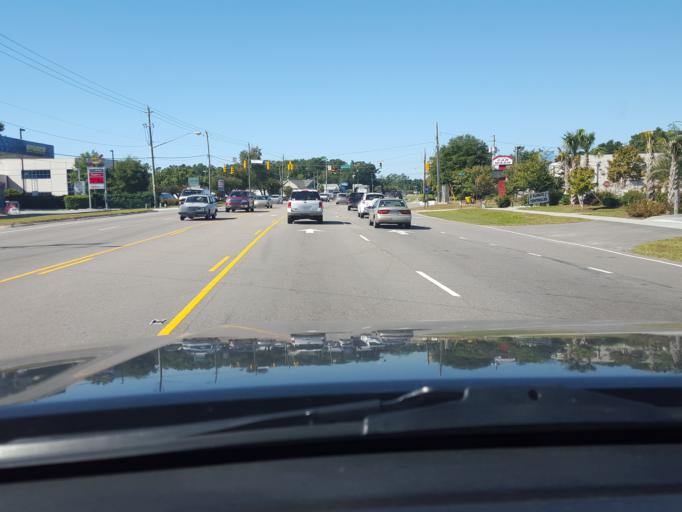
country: US
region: North Carolina
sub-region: New Hanover County
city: Seagate
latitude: 34.2080
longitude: -77.8629
